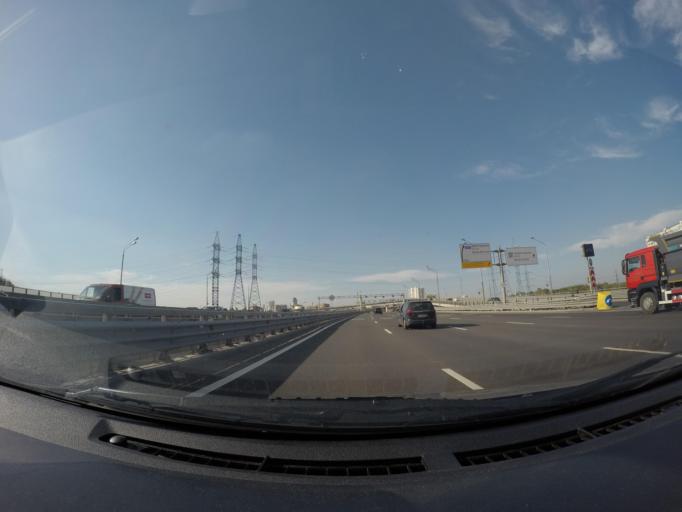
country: RU
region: Moskovskaya
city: Levoberezhnaya
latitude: 55.8811
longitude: 37.4838
